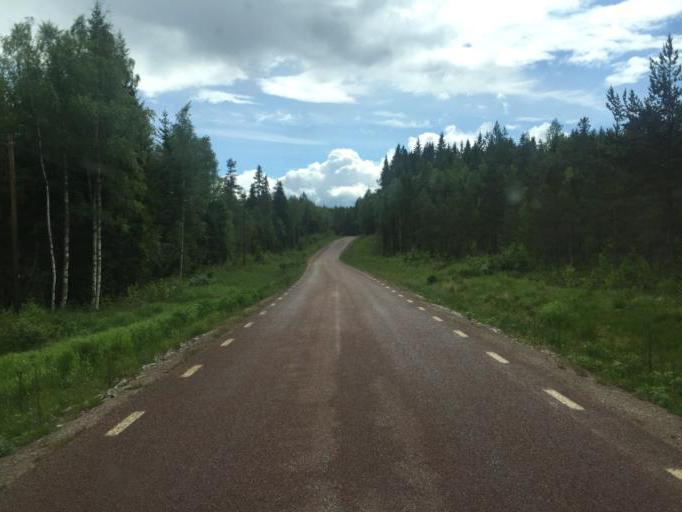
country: SE
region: Vaermland
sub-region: Hagfors Kommun
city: Hagfors
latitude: 60.3285
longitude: 13.8613
